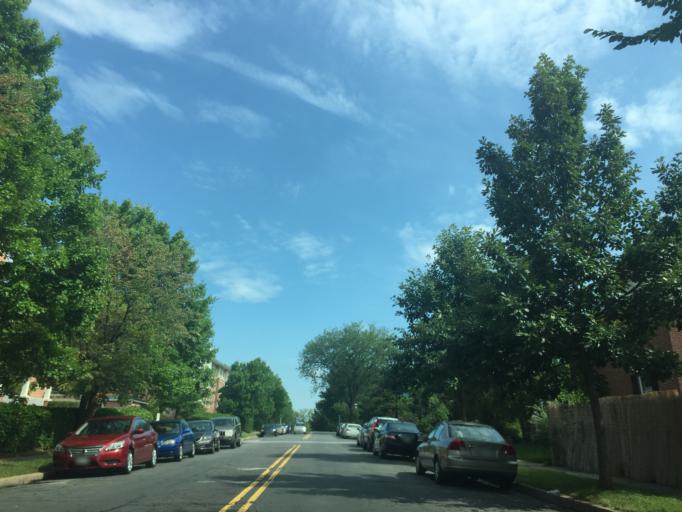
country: US
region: Maryland
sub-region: City of Baltimore
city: Baltimore
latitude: 39.3297
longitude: -76.5993
